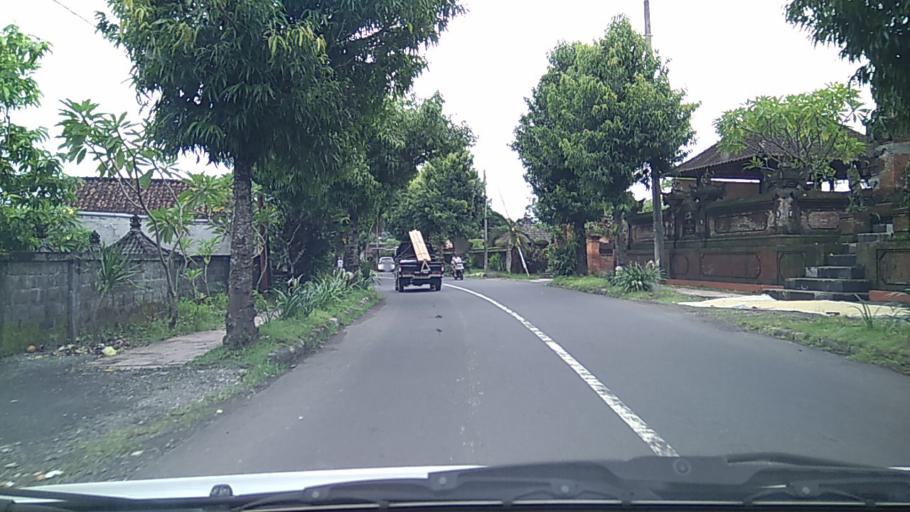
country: ID
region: Bali
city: Banjar Kelodan
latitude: -8.5337
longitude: 115.3483
